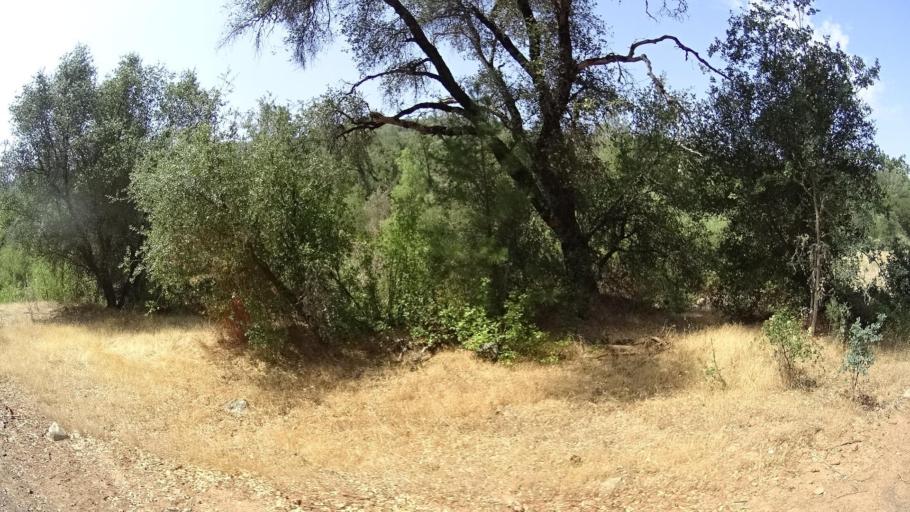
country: US
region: California
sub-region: Mariposa County
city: Midpines
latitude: 37.7038
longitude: -120.1399
